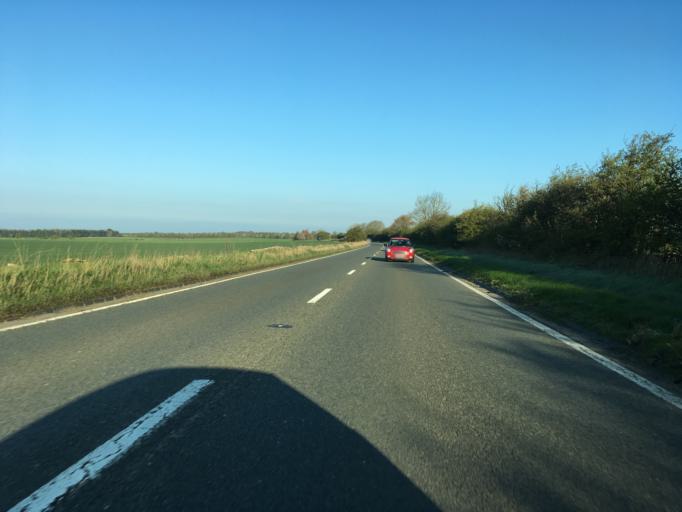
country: GB
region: England
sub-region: Oxfordshire
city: Burford
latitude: 51.8054
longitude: -1.6491
